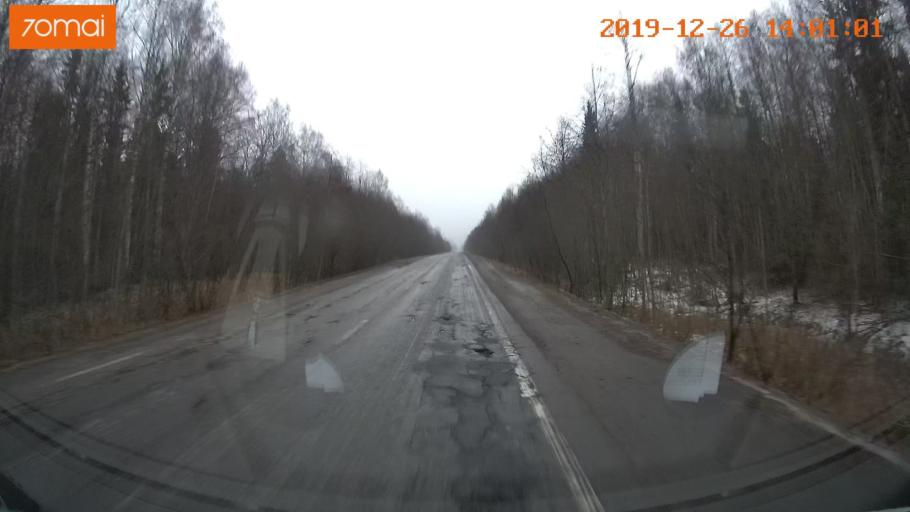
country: RU
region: Jaroslavl
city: Poshekhon'ye
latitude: 58.5536
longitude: 38.7554
